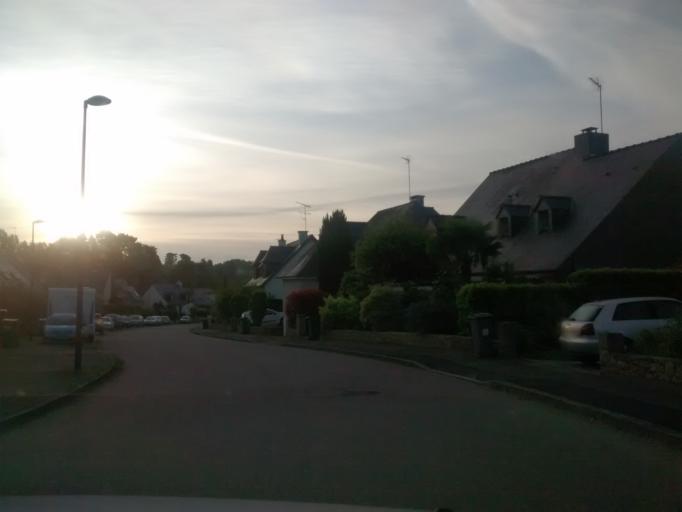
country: FR
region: Brittany
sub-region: Departement d'Ille-et-Vilaine
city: Cesson-Sevigne
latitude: 48.1171
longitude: -1.6268
